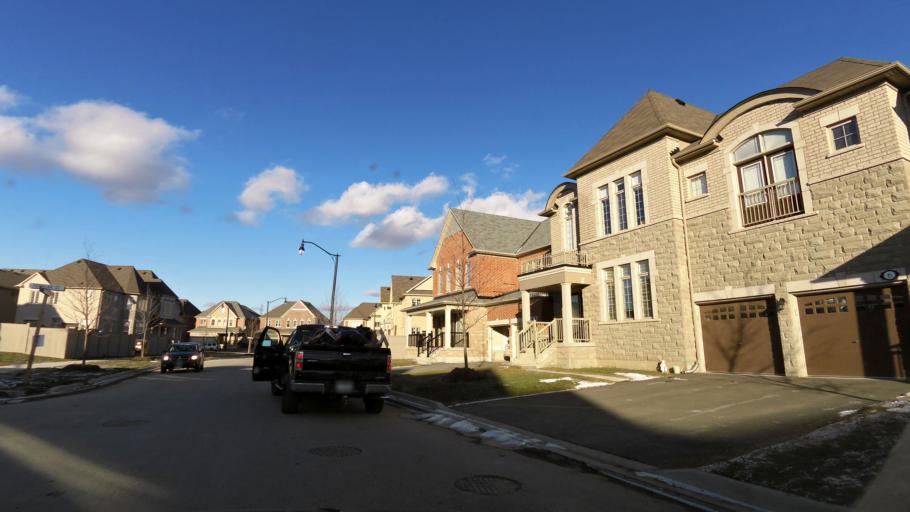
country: CA
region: Ontario
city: Brampton
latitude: 43.6488
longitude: -79.7780
